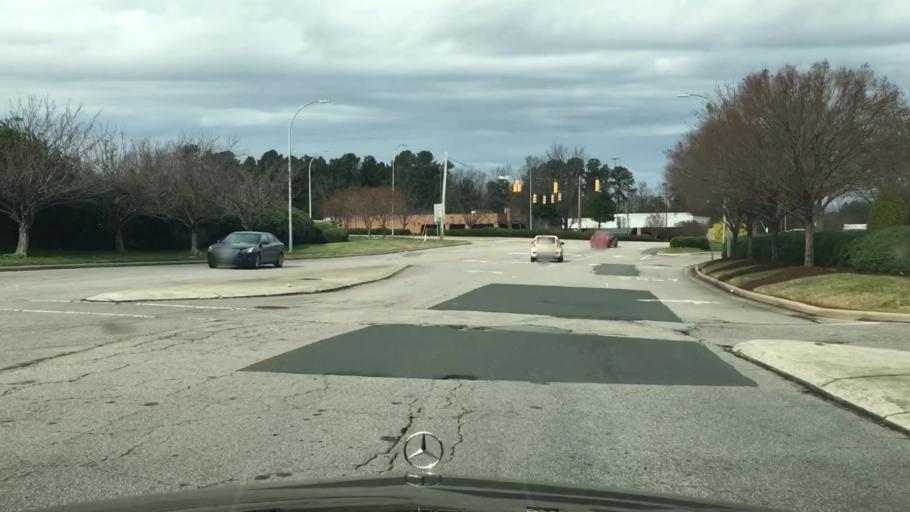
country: US
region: North Carolina
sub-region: Wake County
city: Cary
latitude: 35.7604
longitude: -78.7417
